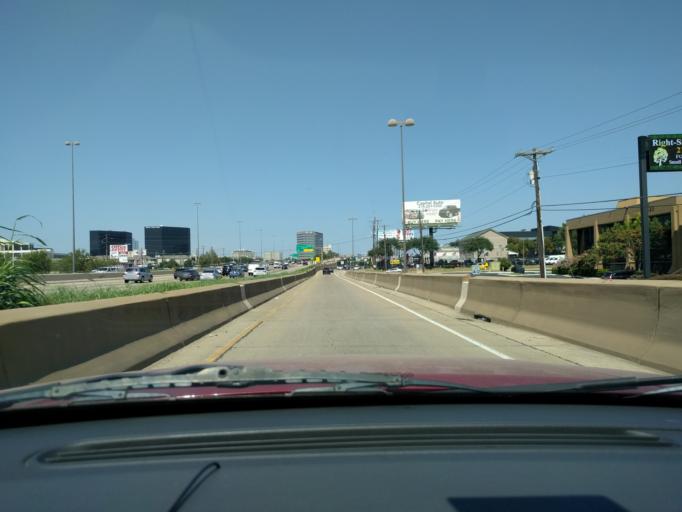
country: US
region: Texas
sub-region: Dallas County
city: Richardson
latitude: 32.9059
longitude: -96.7686
